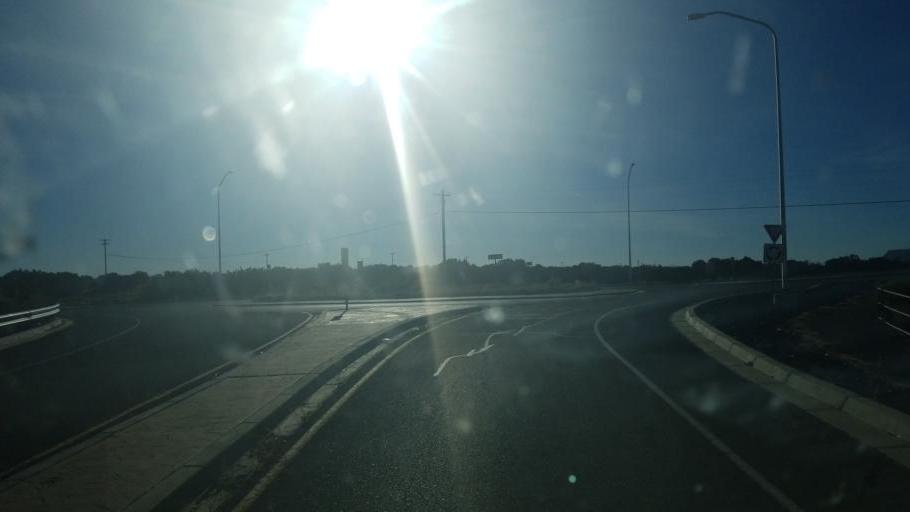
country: US
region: New Mexico
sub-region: Cibola County
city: Skyline-Ganipa
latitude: 35.0715
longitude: -107.5596
